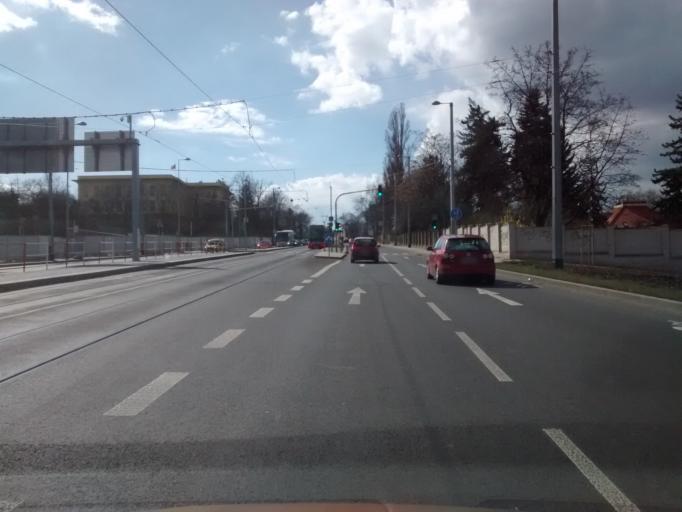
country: CZ
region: Praha
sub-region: Praha 1
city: Mala Strana
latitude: 50.0949
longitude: 14.3958
